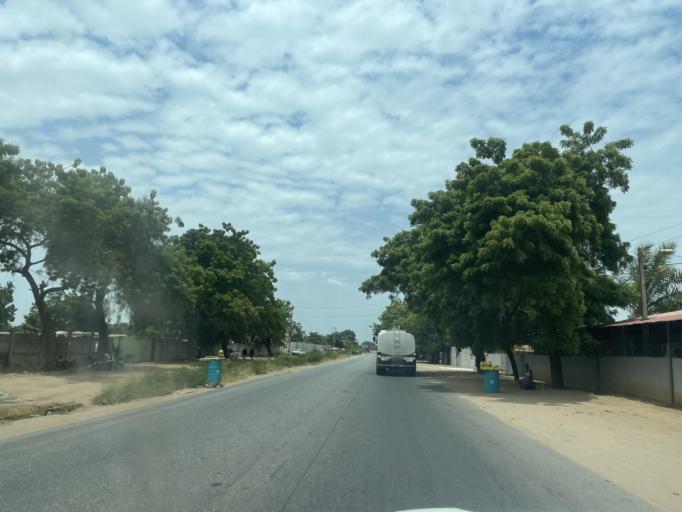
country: AO
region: Luanda
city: Luanda
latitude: -8.9259
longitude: 13.3973
